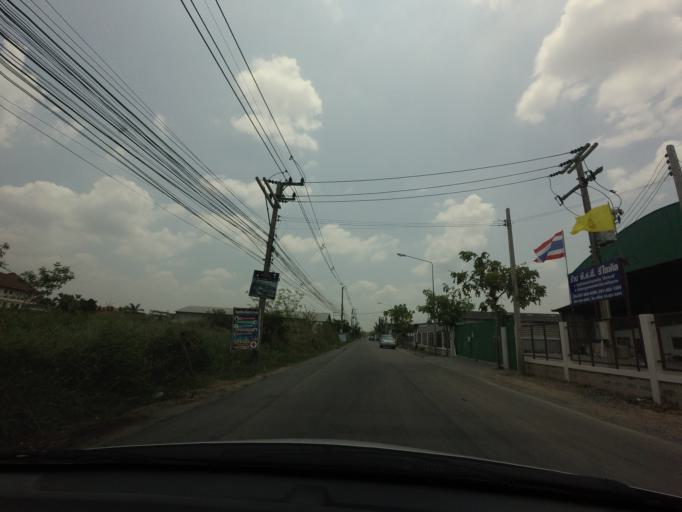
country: TH
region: Pathum Thani
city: Sam Khok
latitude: 14.0440
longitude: 100.5286
